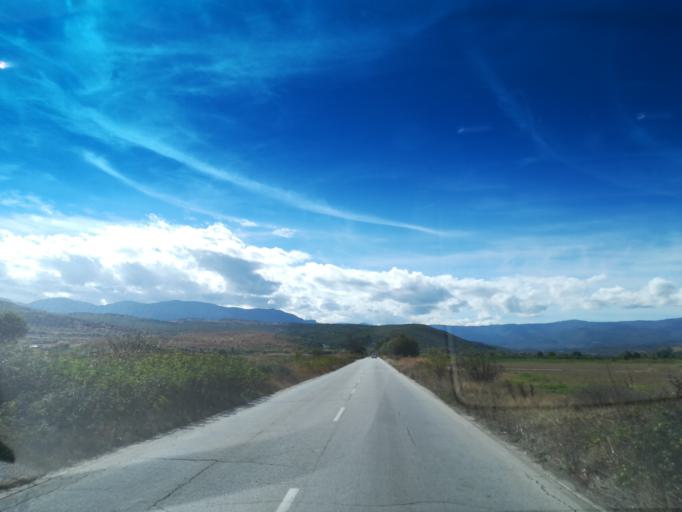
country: BG
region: Plovdiv
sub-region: Obshtina Krichim
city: Krichim
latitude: 42.0778
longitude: 24.4151
